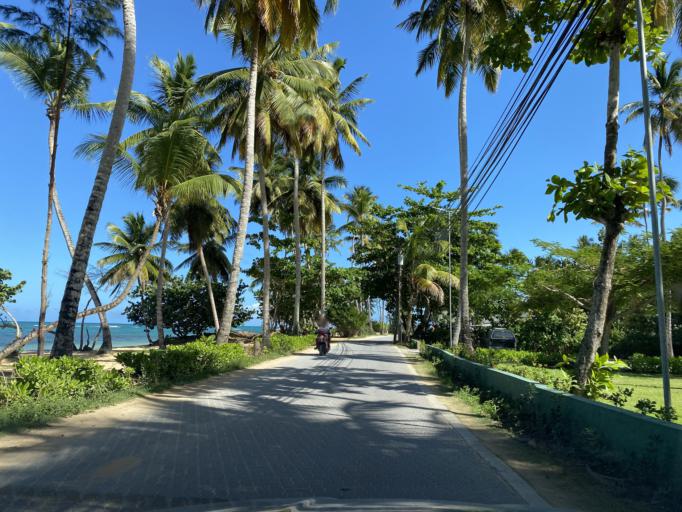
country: DO
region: Samana
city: Las Terrenas
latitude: 19.3264
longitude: -69.5466
